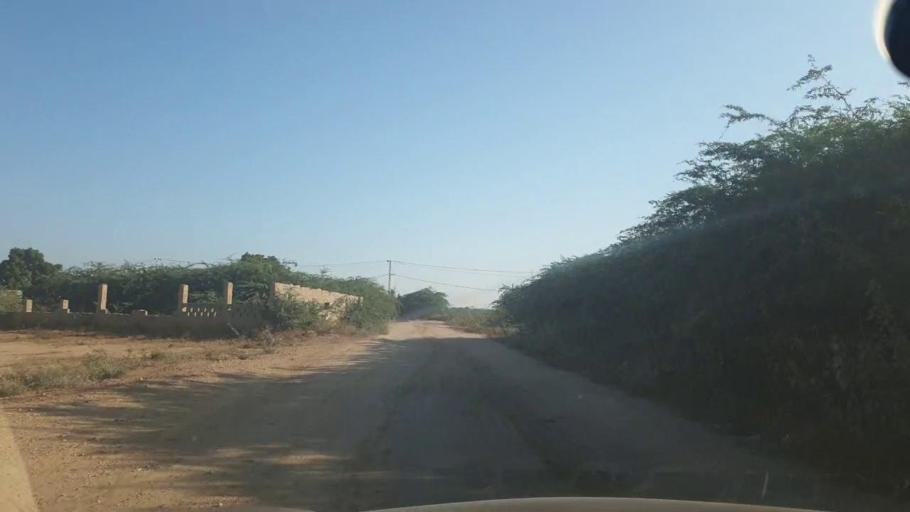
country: PK
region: Sindh
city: Malir Cantonment
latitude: 25.1103
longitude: 67.2660
